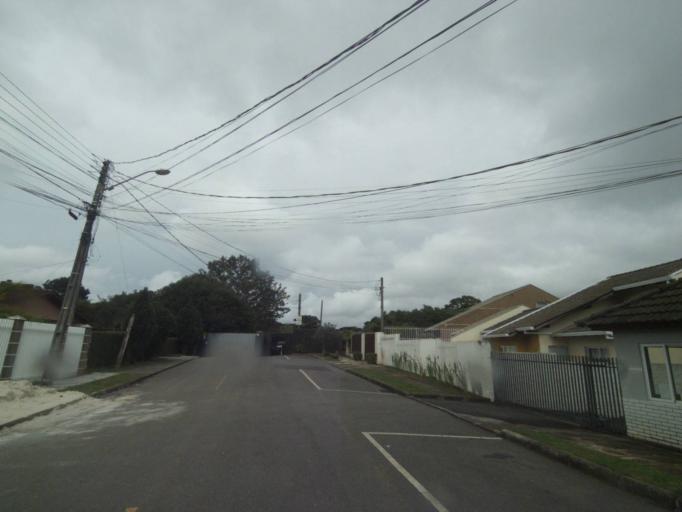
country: BR
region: Parana
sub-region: Curitiba
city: Curitiba
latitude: -25.4481
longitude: -49.3425
